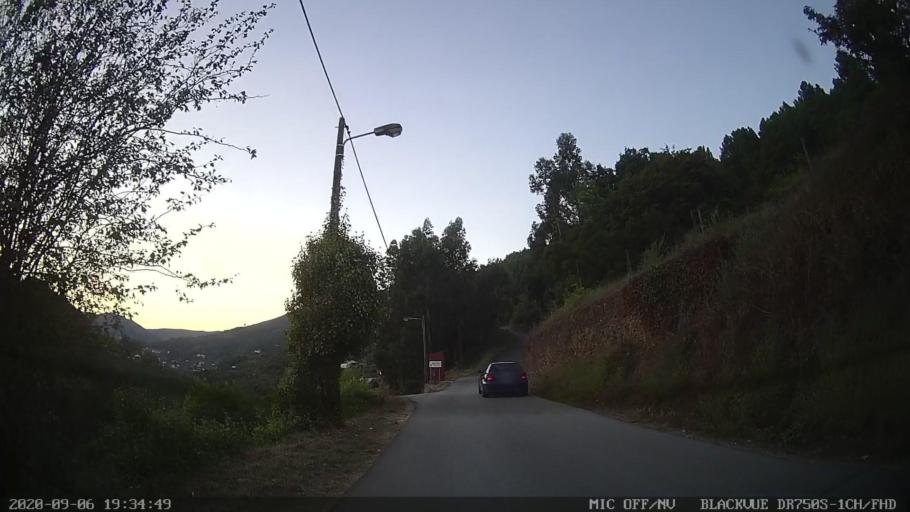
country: PT
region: Vila Real
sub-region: Mesao Frio
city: Mesao Frio
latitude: 41.1698
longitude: -7.8950
